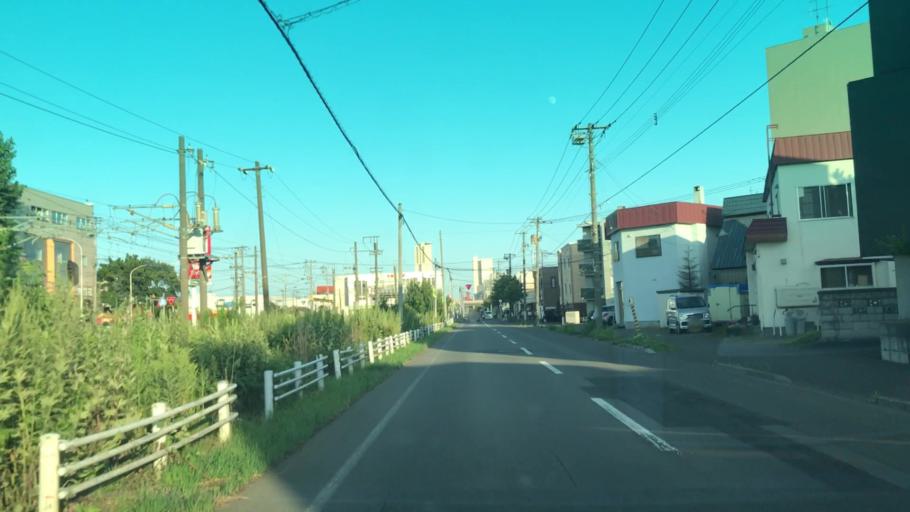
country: JP
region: Hokkaido
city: Sapporo
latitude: 43.0906
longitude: 141.2920
